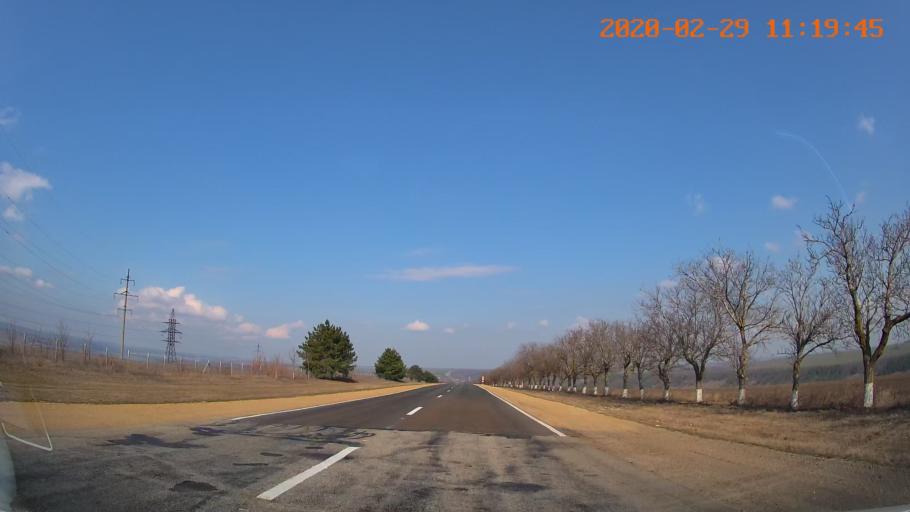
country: MD
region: Telenesti
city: Cocieri
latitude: 47.3549
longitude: 29.1735
